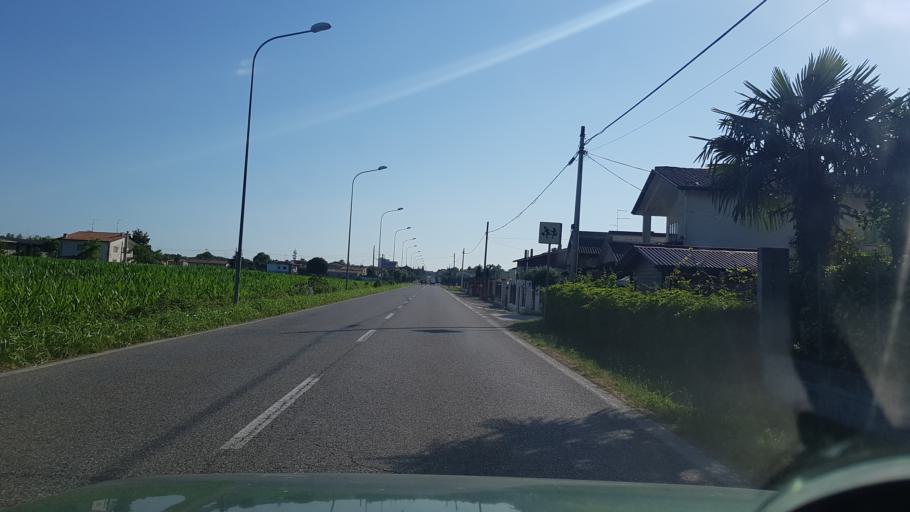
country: IT
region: Friuli Venezia Giulia
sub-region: Provincia di Udine
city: Cervignano del Friuli
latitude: 45.8307
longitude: 13.3495
